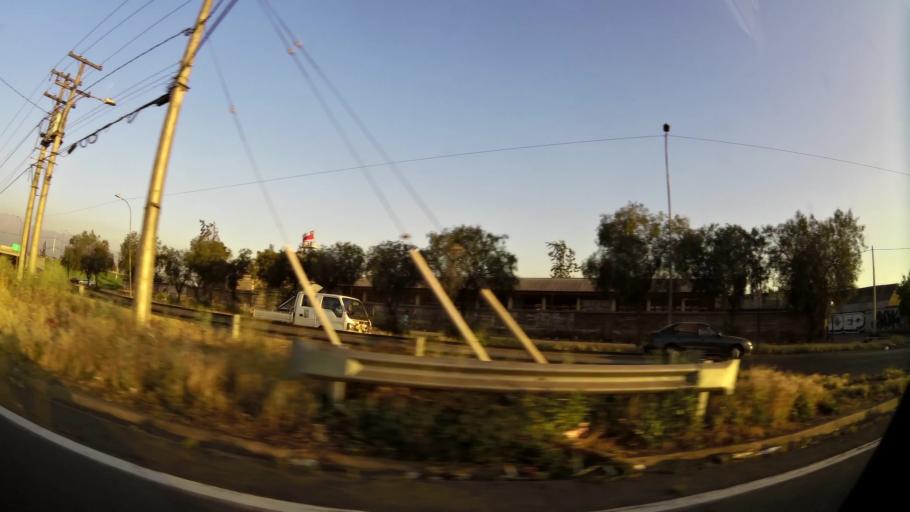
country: CL
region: Santiago Metropolitan
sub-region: Provincia de Santiago
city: Santiago
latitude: -33.4782
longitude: -70.6872
